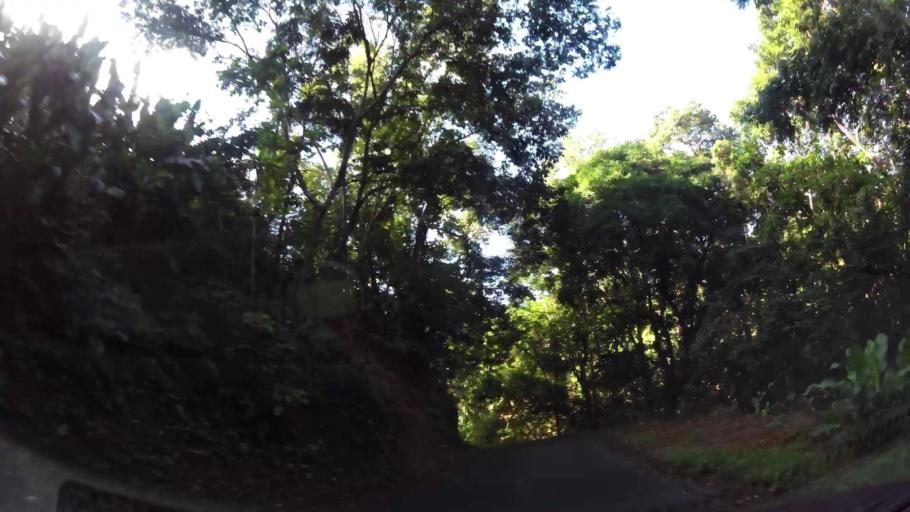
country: DM
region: Saint Andrew
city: Calibishie
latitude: 15.5916
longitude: -61.3587
